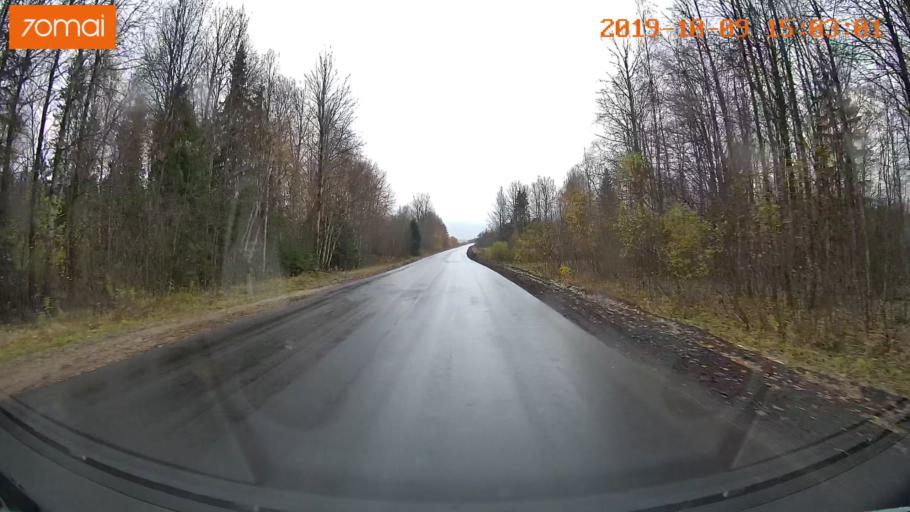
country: RU
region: Kostroma
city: Chistyye Bory
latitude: 58.2772
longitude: 41.6764
